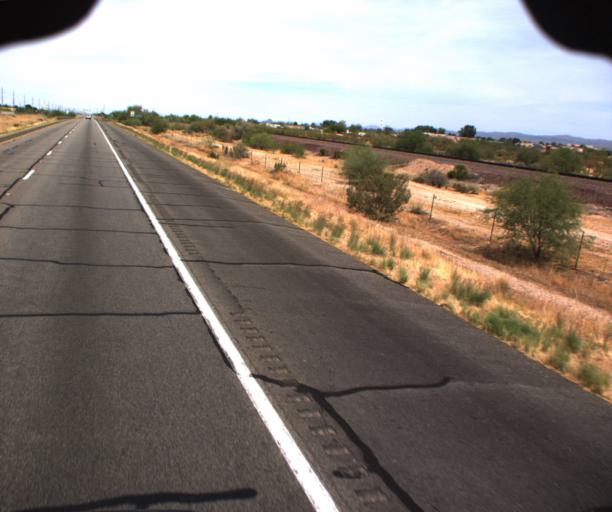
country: US
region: Arizona
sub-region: Maricopa County
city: Sun City West
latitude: 33.7734
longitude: -112.5227
